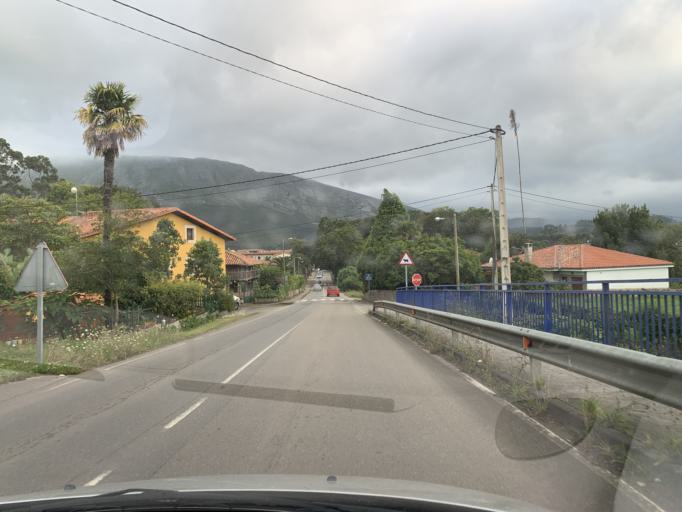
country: ES
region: Asturias
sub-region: Province of Asturias
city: Llanes
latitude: 43.4313
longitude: -4.8616
